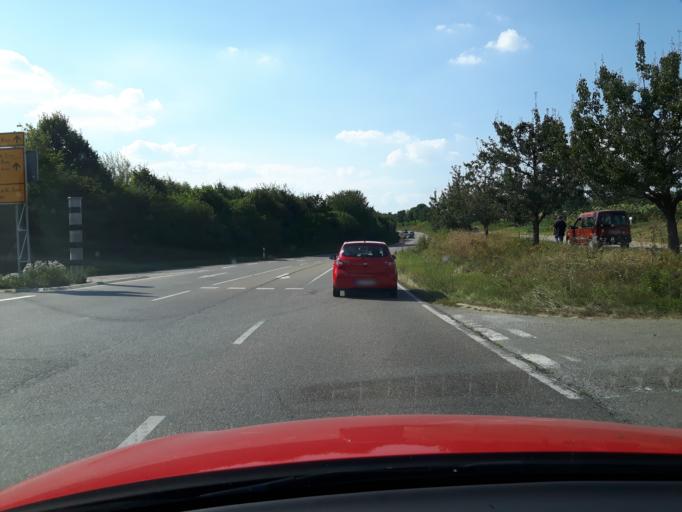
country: DE
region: Baden-Wuerttemberg
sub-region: Regierungsbezirk Stuttgart
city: Nordheim
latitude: 49.1123
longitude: 9.1414
